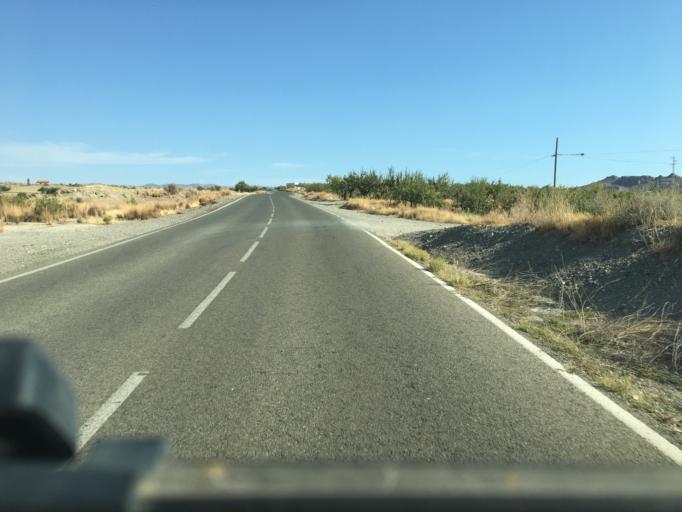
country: ES
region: Andalusia
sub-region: Provincia de Almeria
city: Huercal-Overa
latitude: 37.4350
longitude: -1.9745
